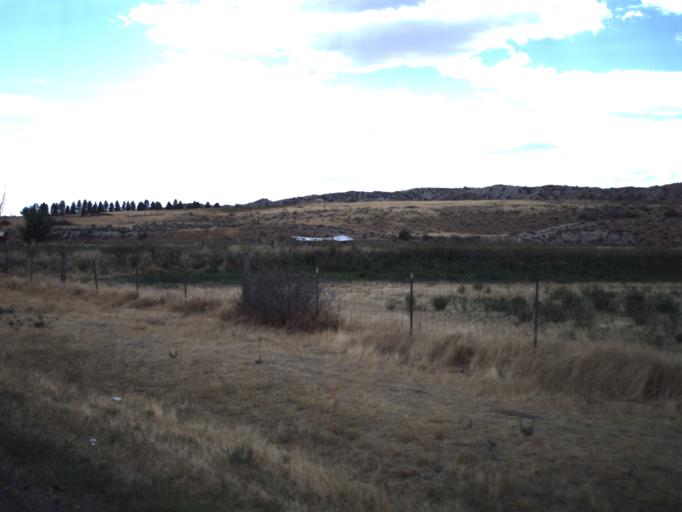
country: US
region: Utah
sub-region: Sanpete County
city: Centerfield
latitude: 39.1215
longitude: -111.7119
